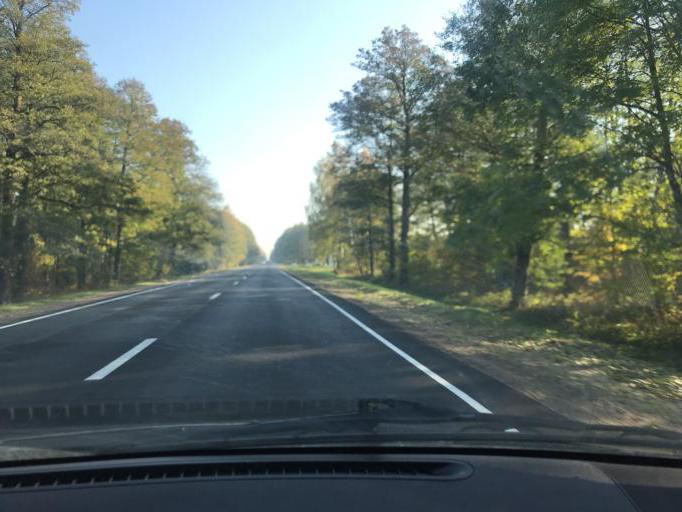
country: BY
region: Brest
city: Baranovichi
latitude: 52.8817
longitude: 25.7752
